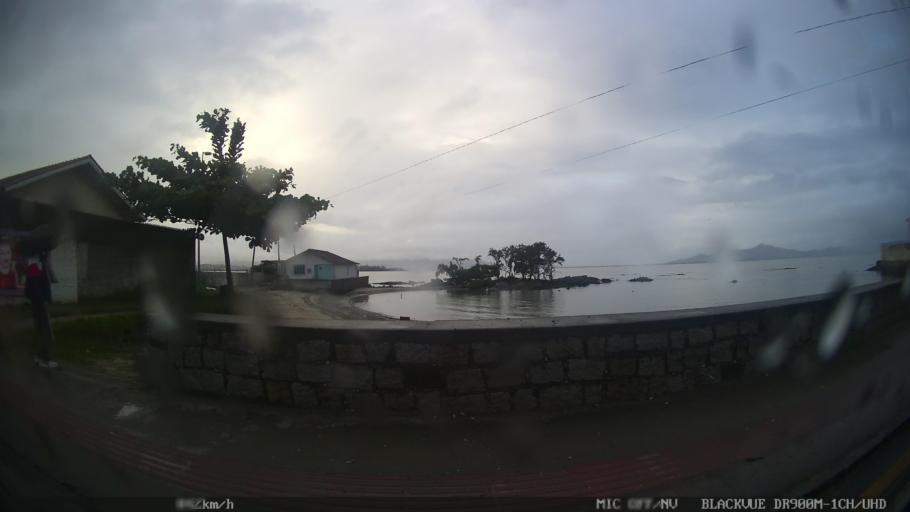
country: BR
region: Santa Catarina
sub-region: Sao Jose
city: Campinas
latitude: -27.6130
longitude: -48.6257
